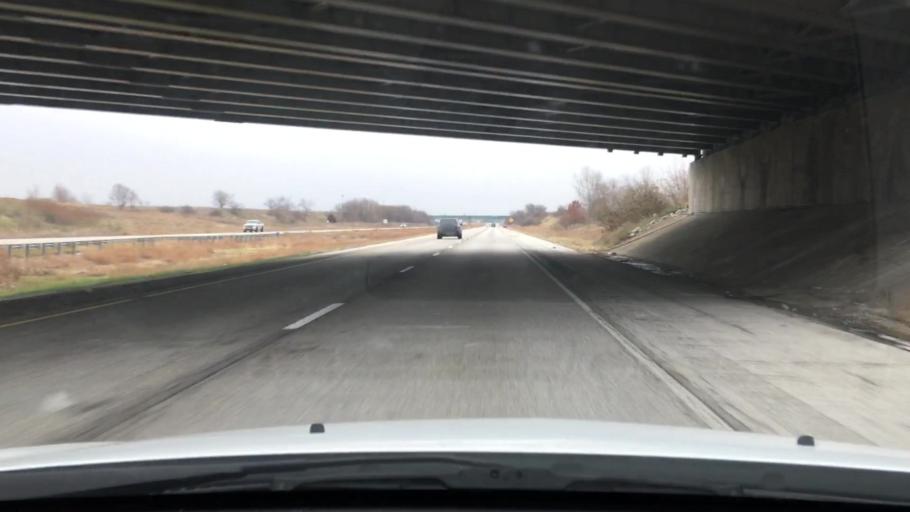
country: US
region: Illinois
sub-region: Morgan County
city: South Jacksonville
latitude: 39.7230
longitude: -90.1677
